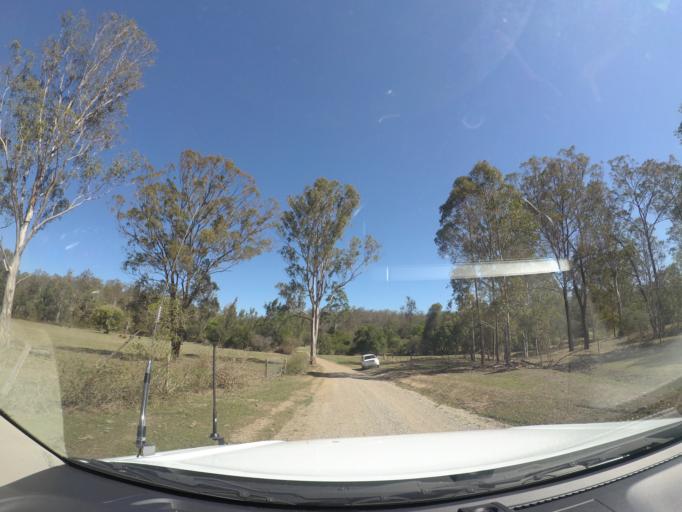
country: AU
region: Queensland
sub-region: Ipswich
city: Springfield Lakes
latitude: -27.7480
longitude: 152.8994
